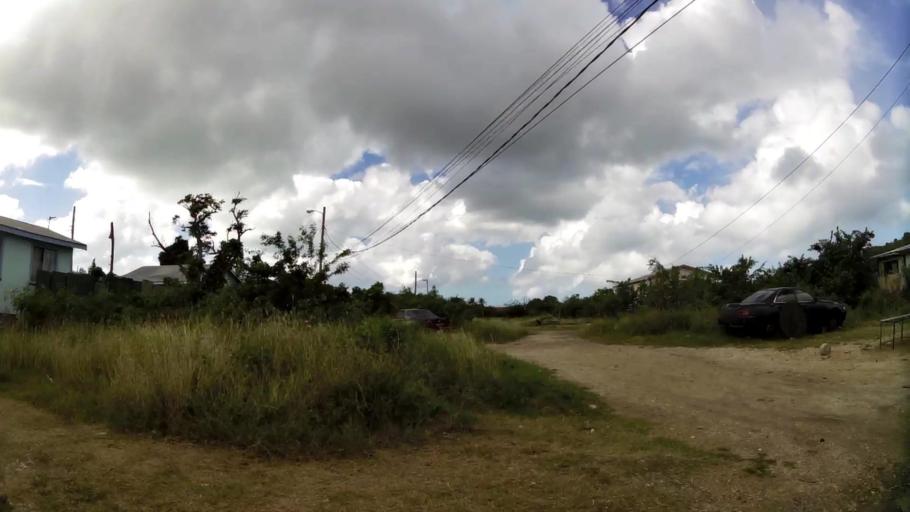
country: AG
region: Saint John
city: Saint John's
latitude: 17.1118
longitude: -61.8544
